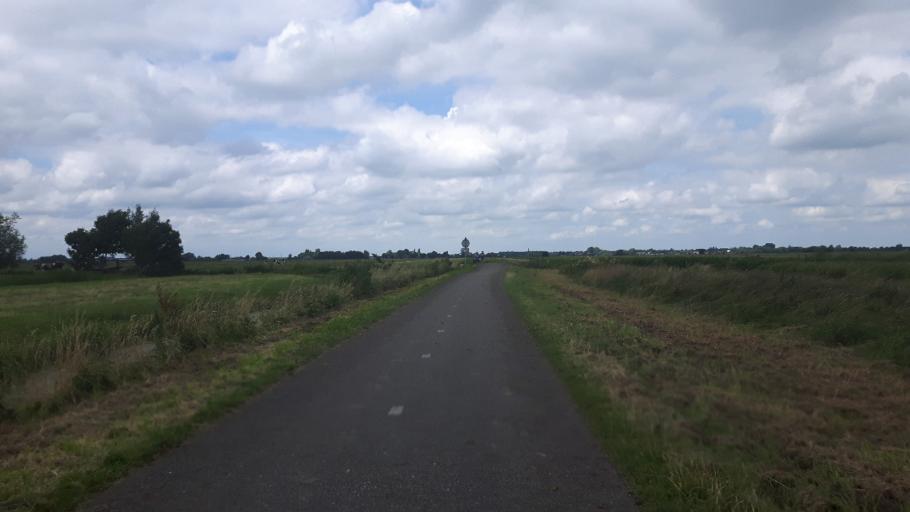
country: NL
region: South Holland
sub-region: Gemeente Vlist
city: Haastrecht
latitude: 51.9417
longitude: 4.7654
